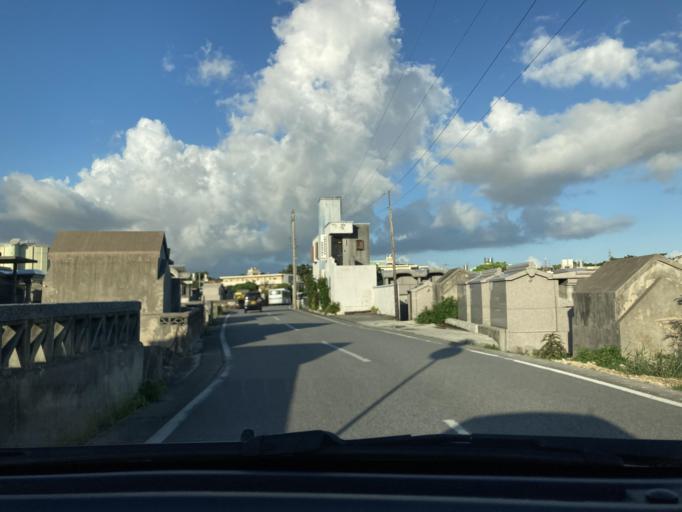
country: JP
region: Okinawa
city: Naha-shi
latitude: 26.2045
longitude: 127.7122
